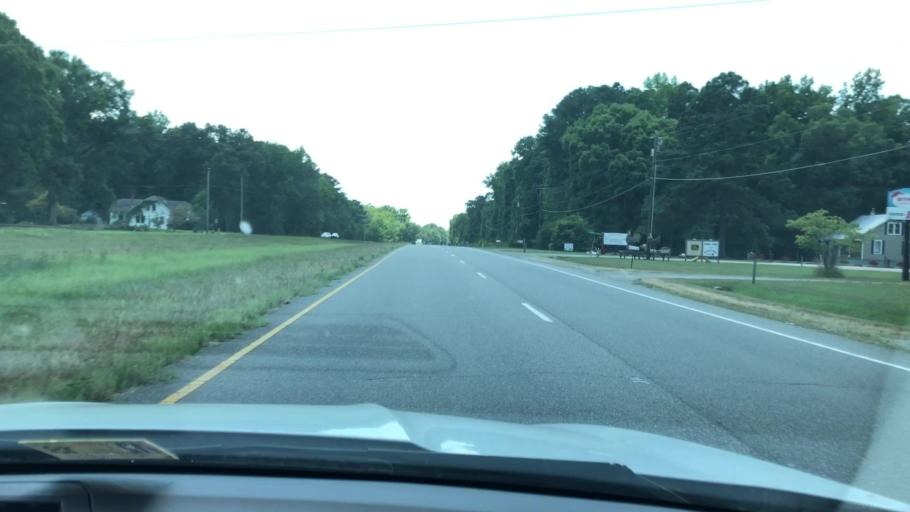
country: US
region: Virginia
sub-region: King William County
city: West Point
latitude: 37.5391
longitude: -76.7597
